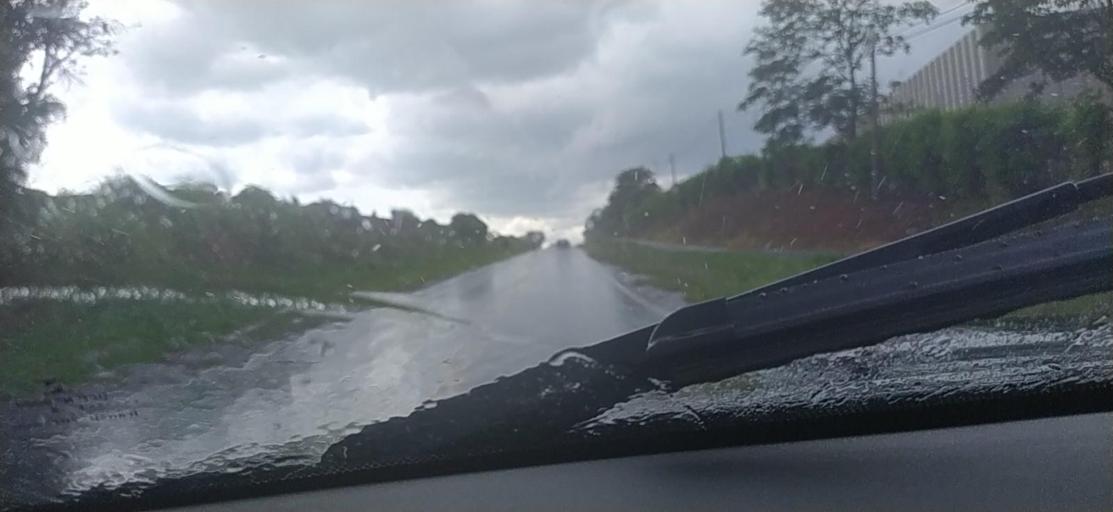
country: BR
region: Sao Paulo
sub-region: Catanduva
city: Catanduva
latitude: -21.1576
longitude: -48.9505
